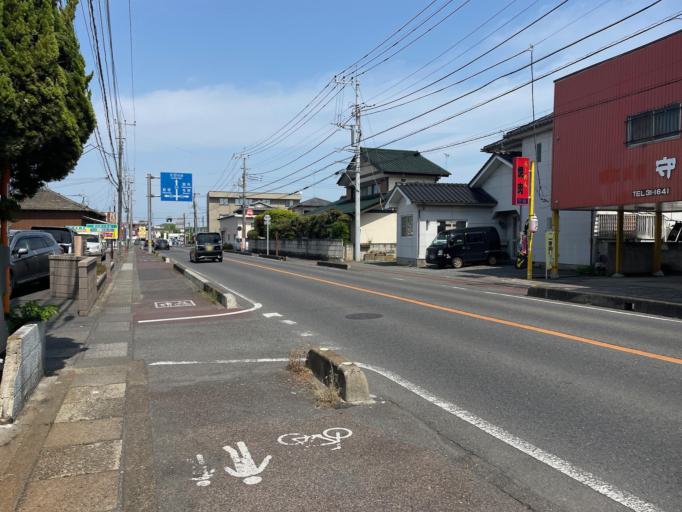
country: JP
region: Gunma
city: Ota
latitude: 36.2943
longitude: 139.3529
